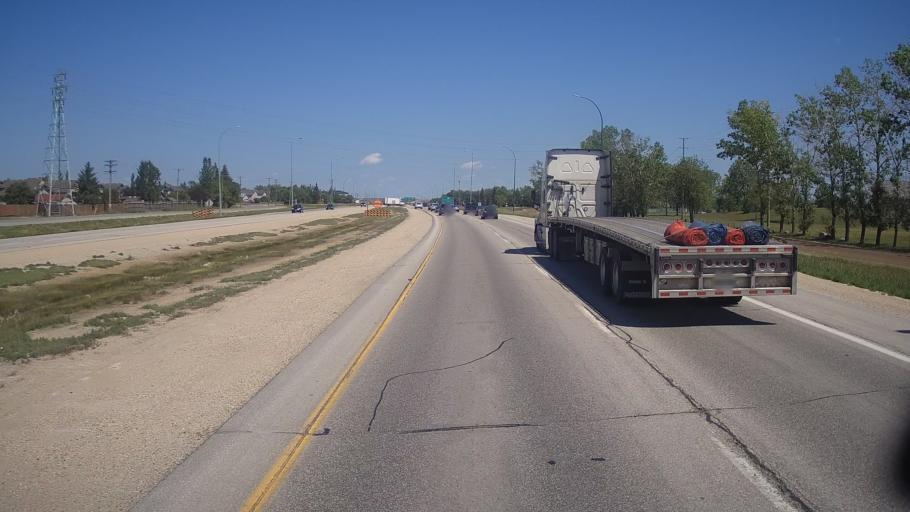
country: CA
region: Manitoba
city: Winnipeg
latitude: 49.9349
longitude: -97.0409
